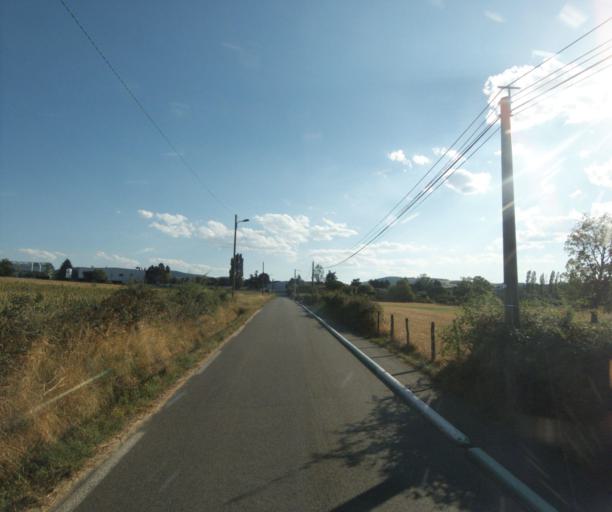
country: FR
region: Rhone-Alpes
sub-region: Departement du Rhone
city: Lentilly
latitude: 45.8279
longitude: 4.6740
